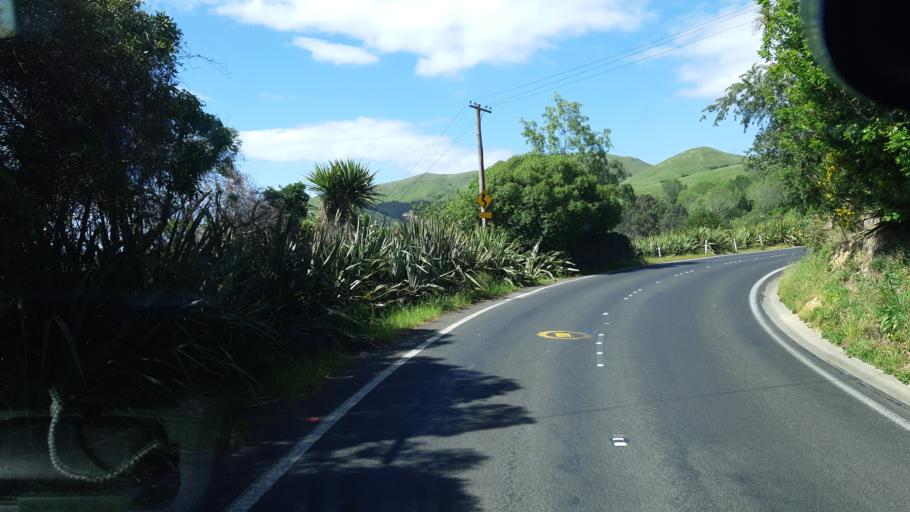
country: NZ
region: Otago
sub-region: Dunedin City
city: Portobello
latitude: -45.8382
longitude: 170.6560
